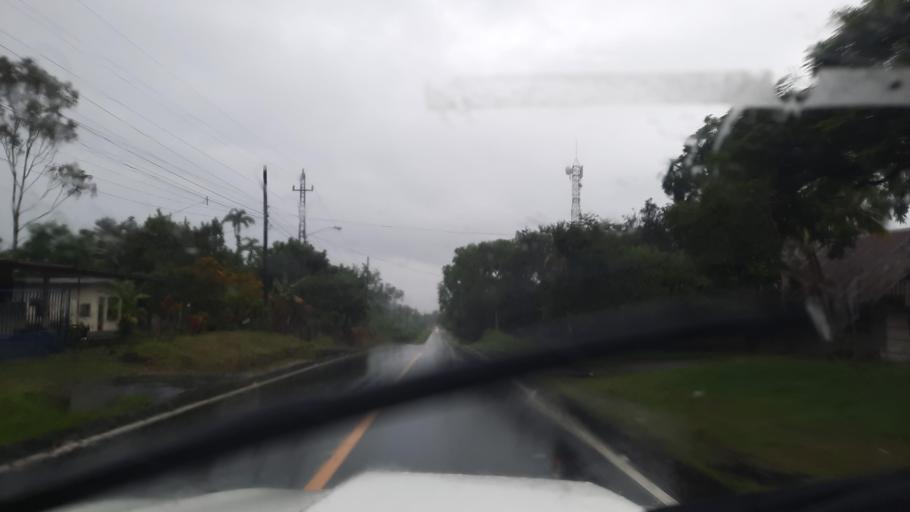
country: PA
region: Chiriqui
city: Sortova
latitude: 8.5841
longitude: -82.6371
